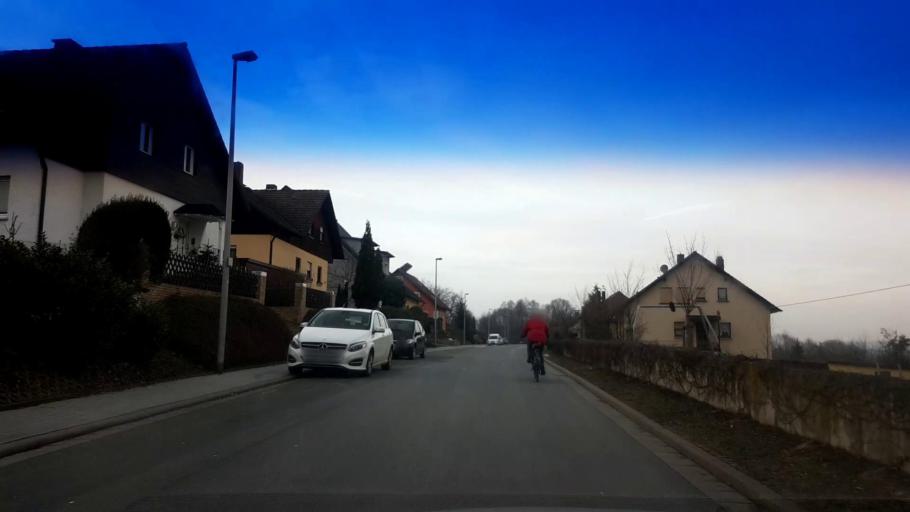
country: DE
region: Bavaria
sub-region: Upper Franconia
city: Altendorf
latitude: 49.7942
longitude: 10.9972
